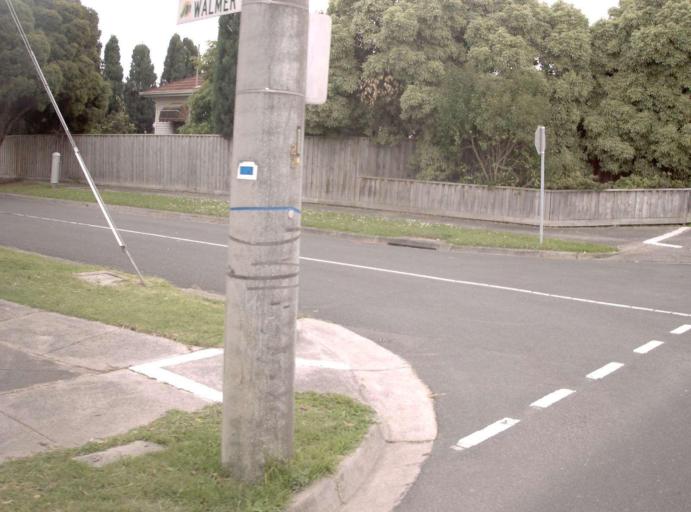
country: AU
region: Victoria
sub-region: Maroondah
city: Heathmont
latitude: -37.8261
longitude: 145.2273
